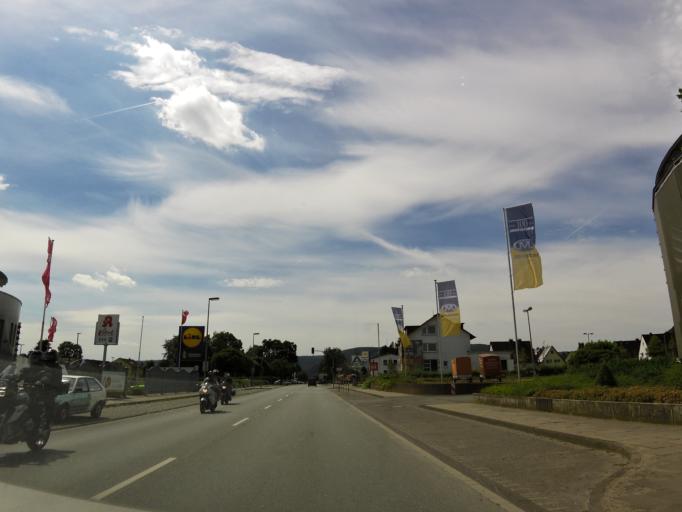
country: DE
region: North Rhine-Westphalia
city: Beverungen
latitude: 51.6739
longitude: 9.3755
